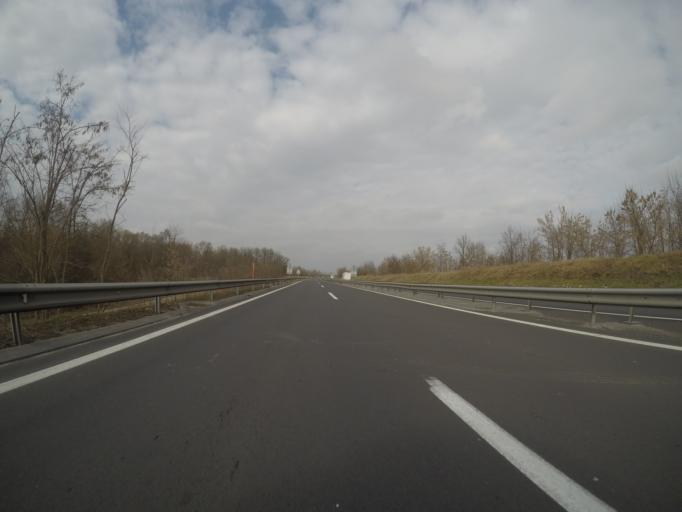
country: SI
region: Murska Sobota
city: Bakovci
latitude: 46.6125
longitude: 16.1302
